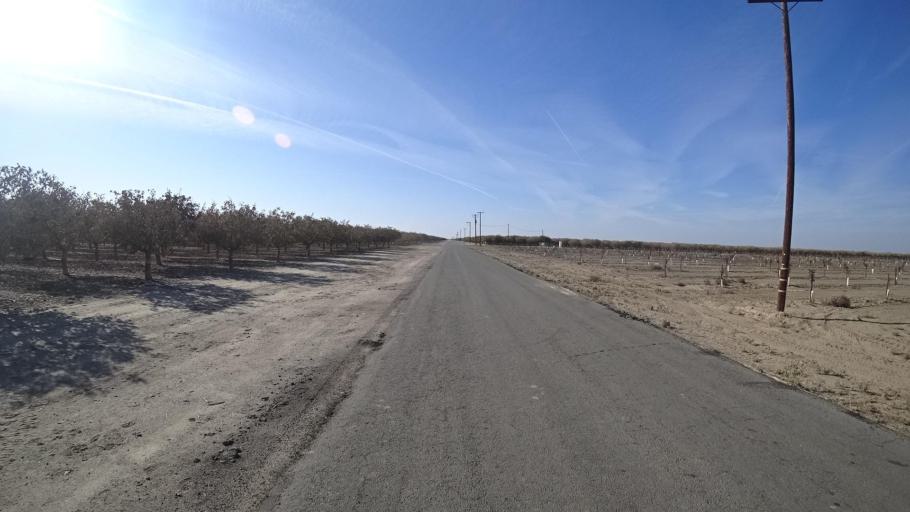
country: US
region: California
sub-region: Kern County
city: Wasco
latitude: 35.6885
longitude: -119.4224
